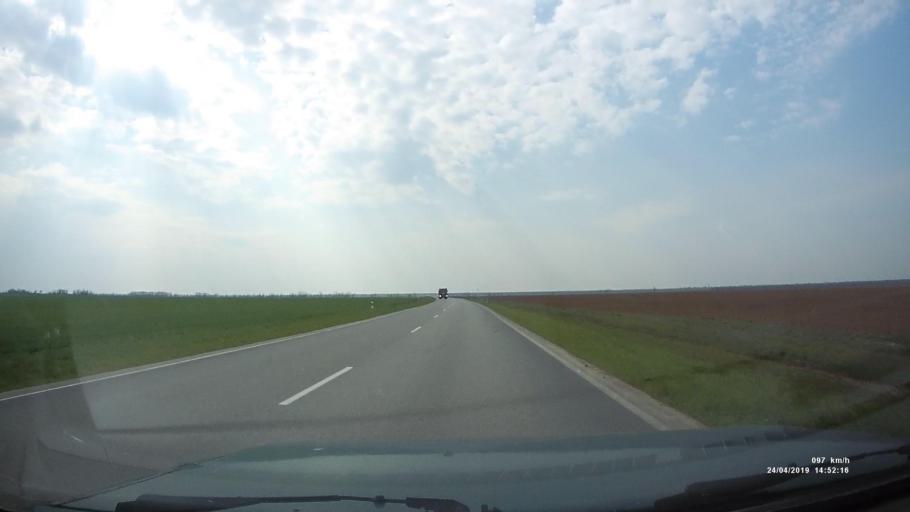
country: RU
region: Rostov
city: Remontnoye
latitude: 46.5300
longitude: 43.6841
